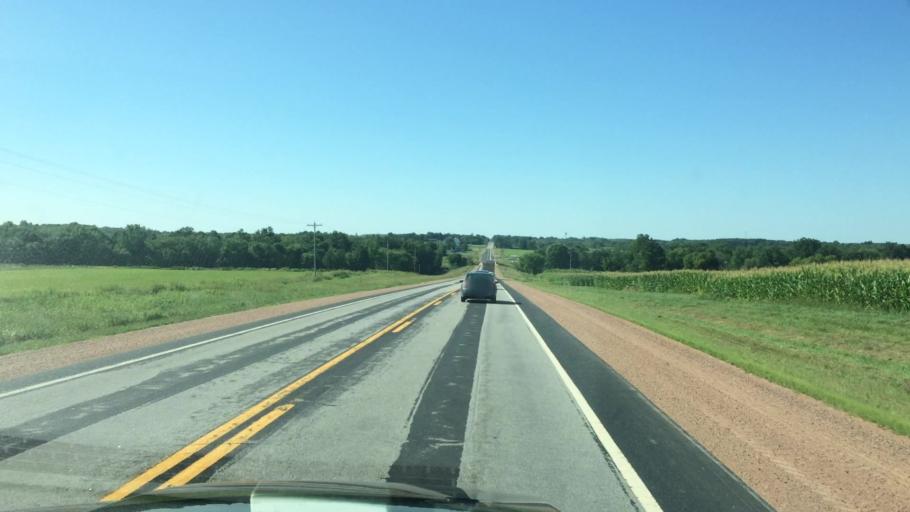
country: US
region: Wisconsin
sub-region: Marathon County
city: Stratford
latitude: 44.8276
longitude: -90.0792
